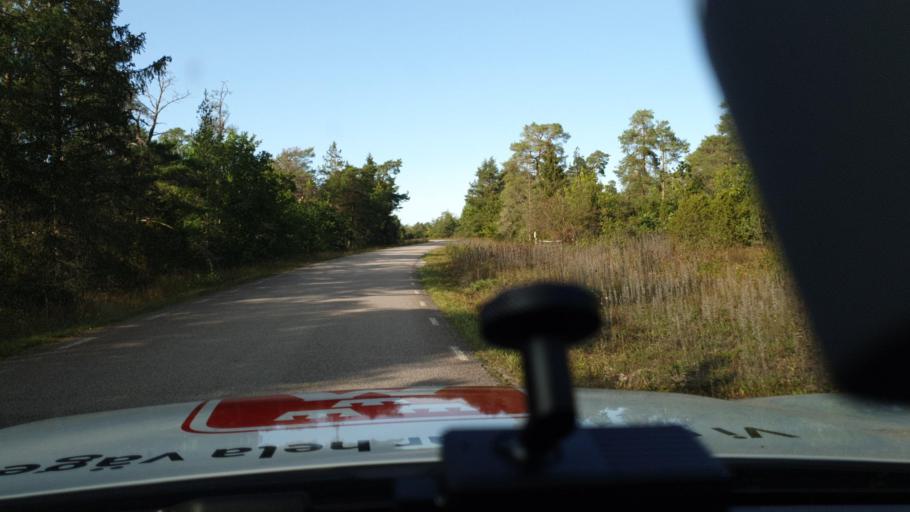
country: SE
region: Gotland
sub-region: Gotland
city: Slite
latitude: 57.6860
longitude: 18.6375
